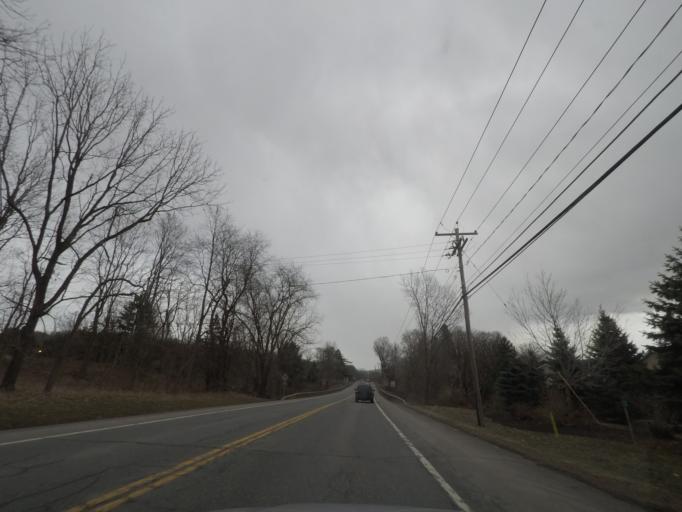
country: US
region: New York
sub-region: Onondaga County
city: Fayetteville
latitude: 43.0333
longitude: -75.9840
